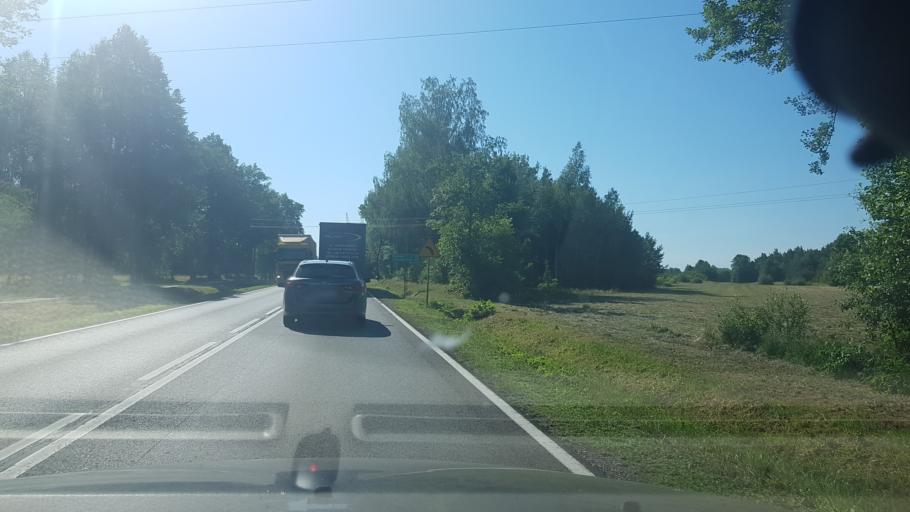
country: PL
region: Masovian Voivodeship
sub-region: Powiat wegrowski
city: Lochow
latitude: 52.5412
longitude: 21.6493
